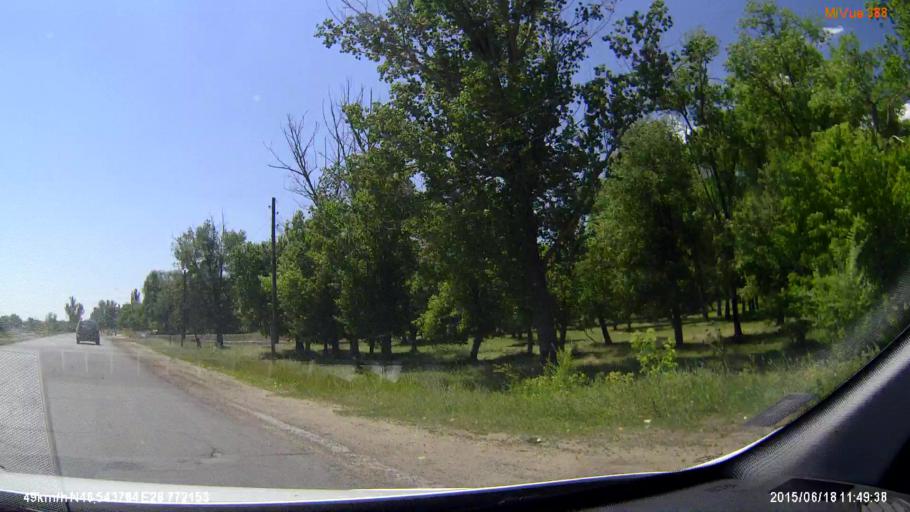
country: MD
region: Cimislia
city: Cimislia
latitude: 46.5440
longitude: 28.7720
